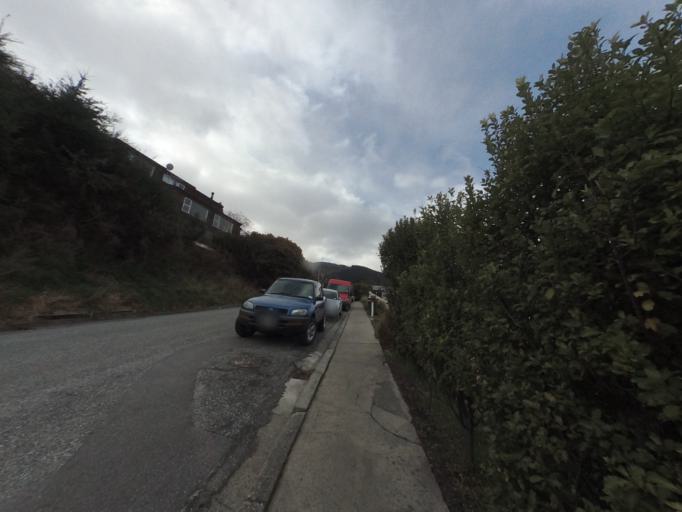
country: NZ
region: Otago
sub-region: Queenstown-Lakes District
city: Queenstown
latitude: -45.0404
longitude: 168.6335
